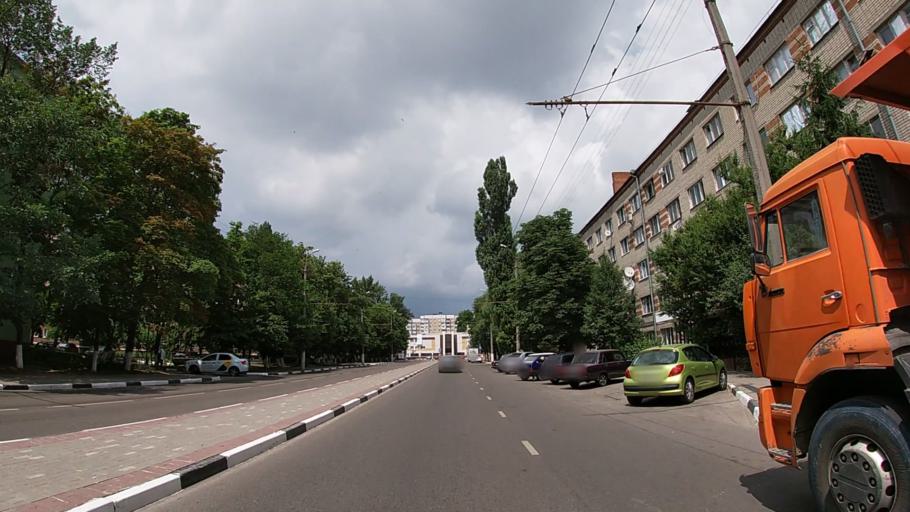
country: RU
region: Belgorod
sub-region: Belgorodskiy Rayon
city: Belgorod
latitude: 50.6115
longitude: 36.5913
